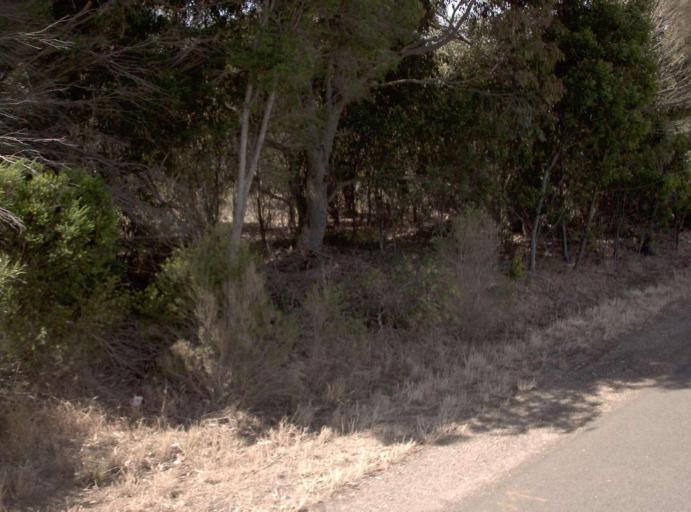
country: AU
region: Victoria
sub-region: Wellington
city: Sale
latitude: -38.1003
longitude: 146.9632
